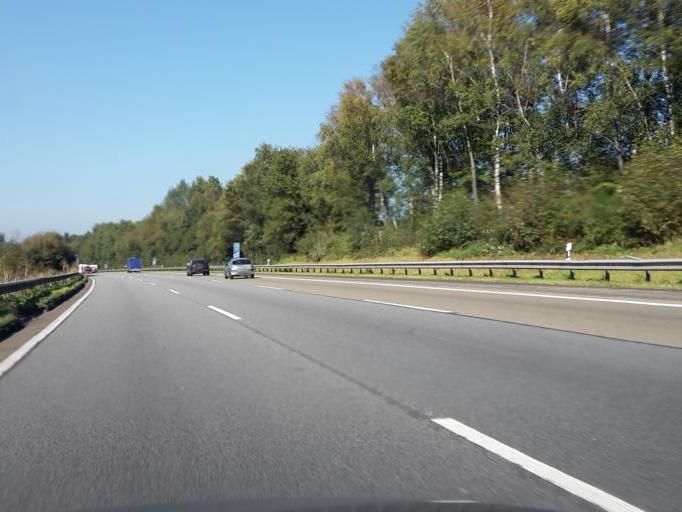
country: DE
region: Rheinland-Pfalz
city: Ebernhahn
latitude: 50.4793
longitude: 7.7580
